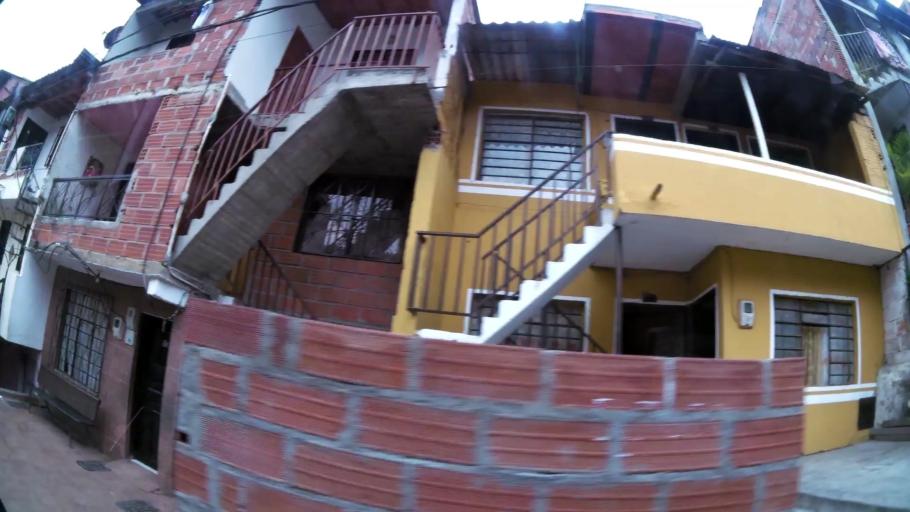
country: CO
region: Antioquia
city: Bello
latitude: 6.3050
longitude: -75.5540
